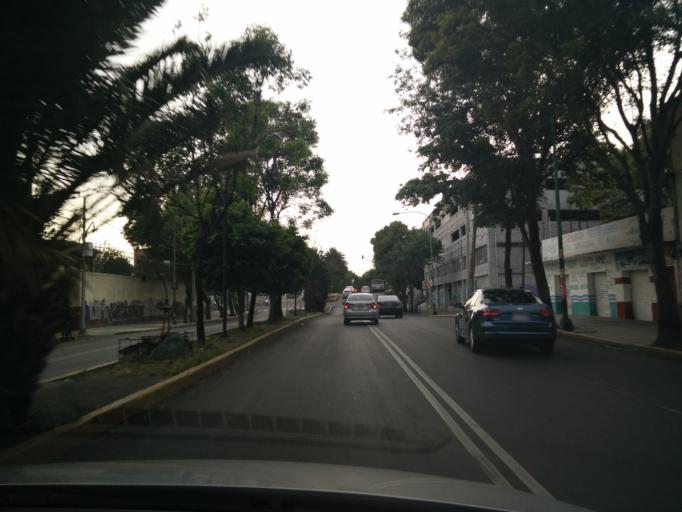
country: MX
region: Mexico City
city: Benito Juarez
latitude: 19.4053
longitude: -99.1500
